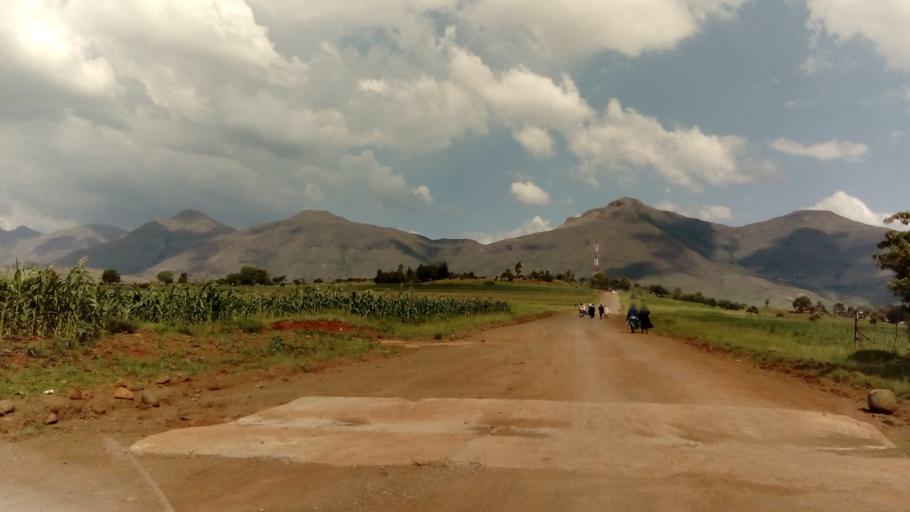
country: LS
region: Maseru
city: Nako
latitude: -29.3924
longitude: 27.8186
